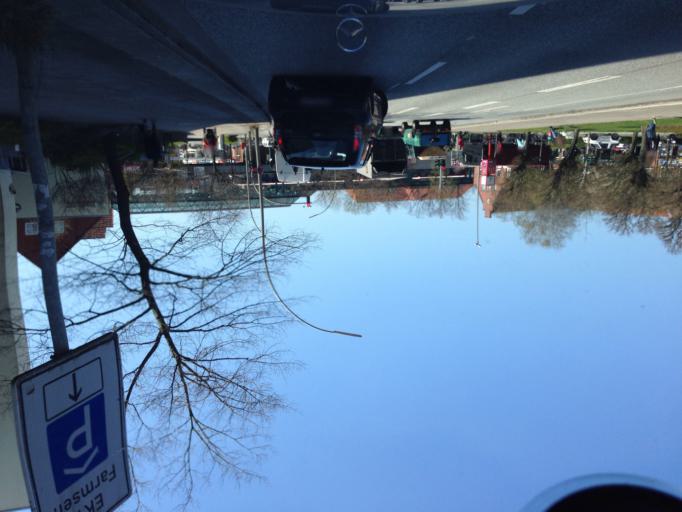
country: DE
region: Hamburg
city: Farmsen-Berne
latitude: 53.6074
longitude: 10.1156
